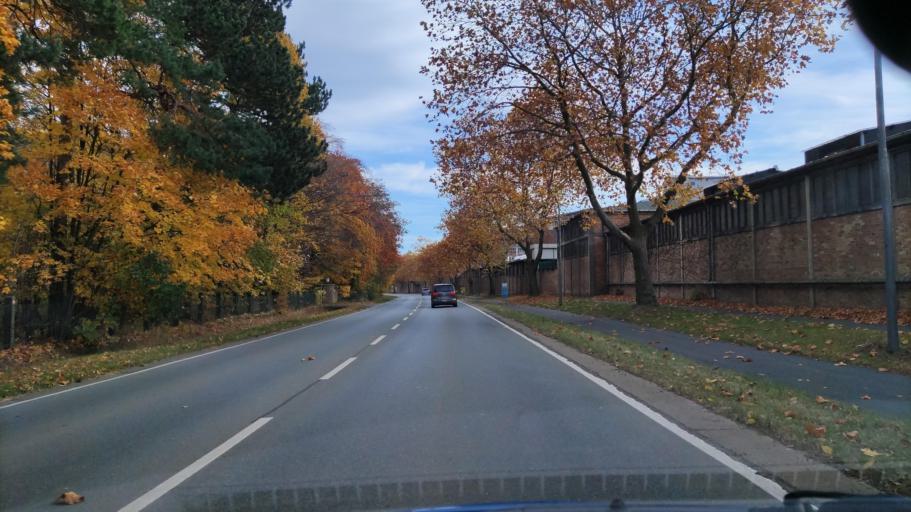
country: DE
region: Lower Saxony
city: Goslar
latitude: 51.9108
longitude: 10.4665
